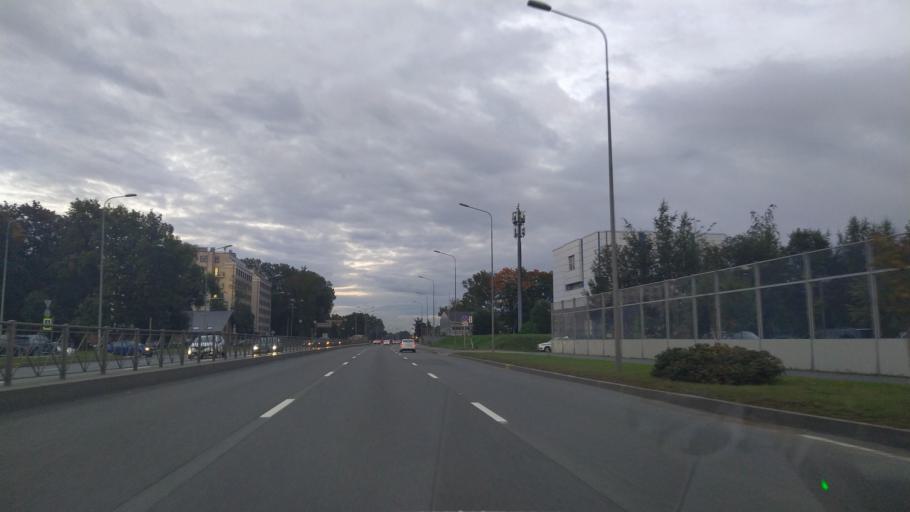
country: RU
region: St.-Petersburg
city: Staraya Derevnya
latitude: 59.9832
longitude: 30.2452
